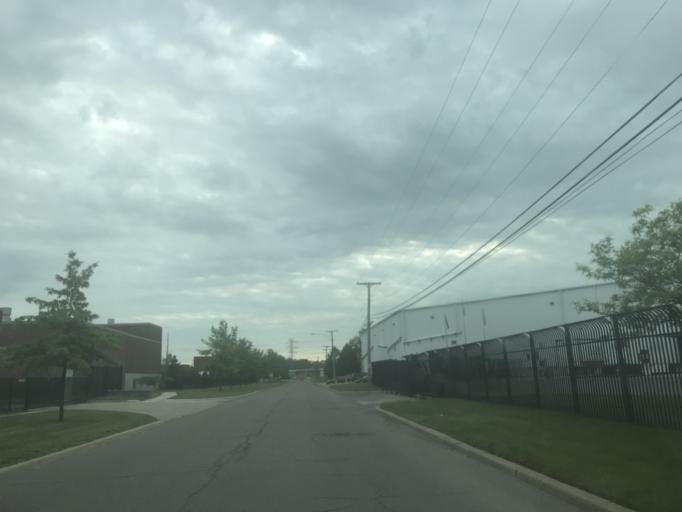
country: US
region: Michigan
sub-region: Wayne County
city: Riverview
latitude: 42.1872
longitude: -83.1632
